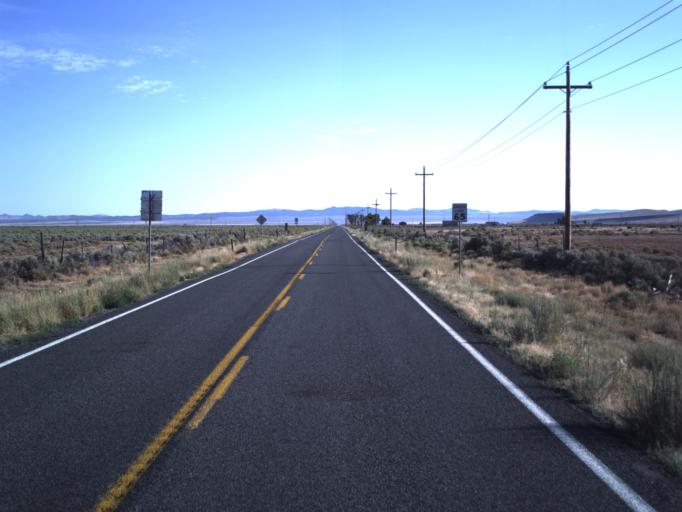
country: US
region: Utah
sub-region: Iron County
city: Enoch
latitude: 37.7876
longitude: -113.0507
